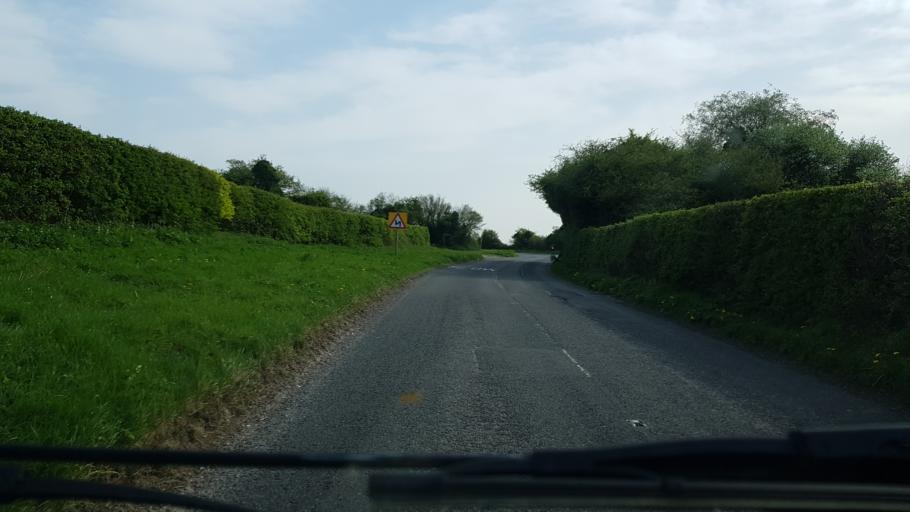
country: GB
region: England
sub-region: Hampshire
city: Overton
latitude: 51.2633
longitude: -1.2646
